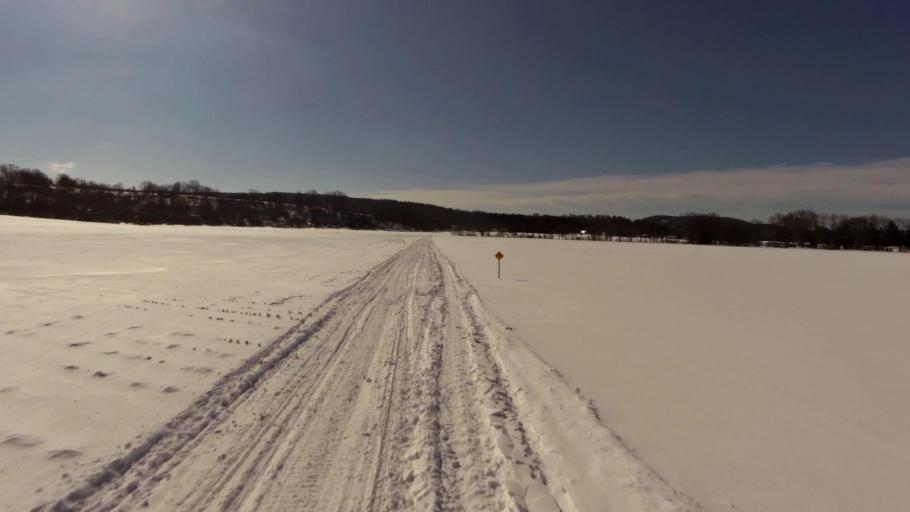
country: US
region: New York
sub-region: Cattaraugus County
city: Franklinville
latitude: 42.3519
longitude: -78.4502
